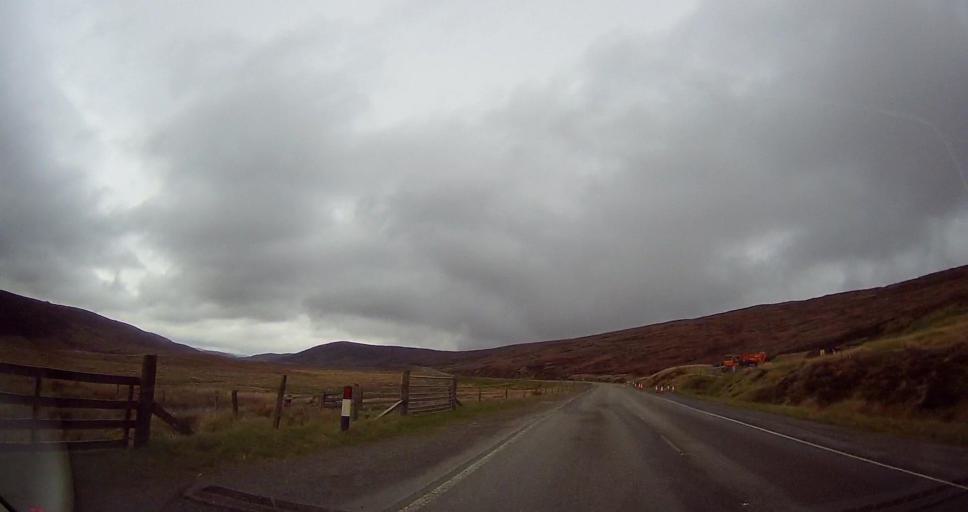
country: GB
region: Scotland
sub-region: Shetland Islands
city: Lerwick
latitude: 60.2842
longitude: -1.2434
